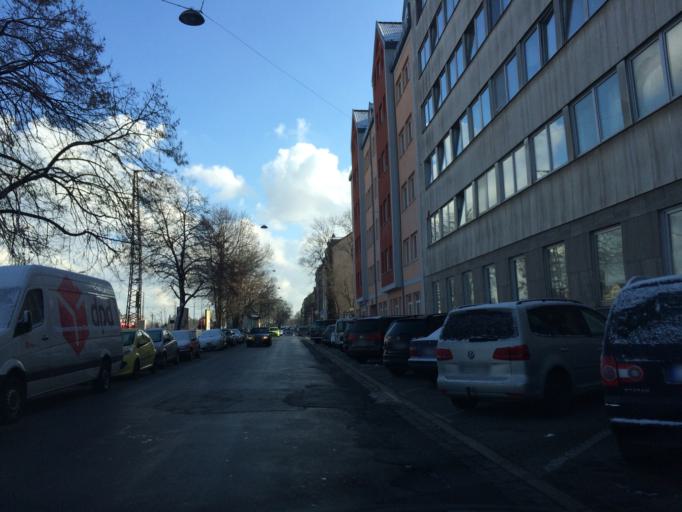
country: DE
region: Bavaria
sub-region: Regierungsbezirk Mittelfranken
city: Furth
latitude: 49.4675
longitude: 10.9979
